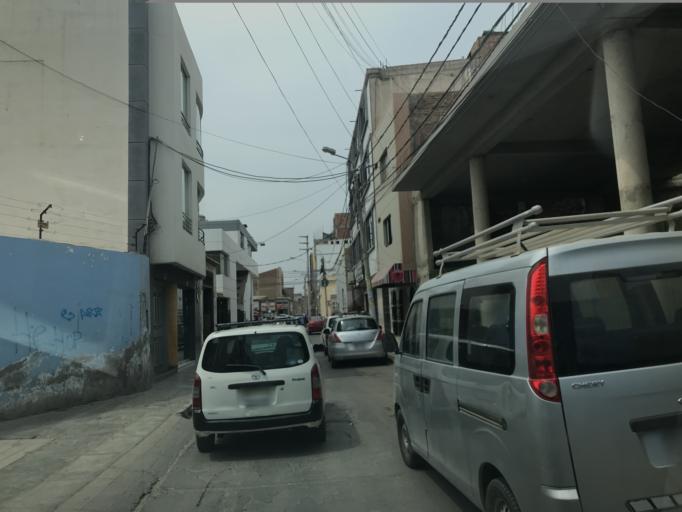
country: PE
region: Lambayeque
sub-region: Provincia de Chiclayo
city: Chiclayo
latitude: -6.7727
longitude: -79.8372
